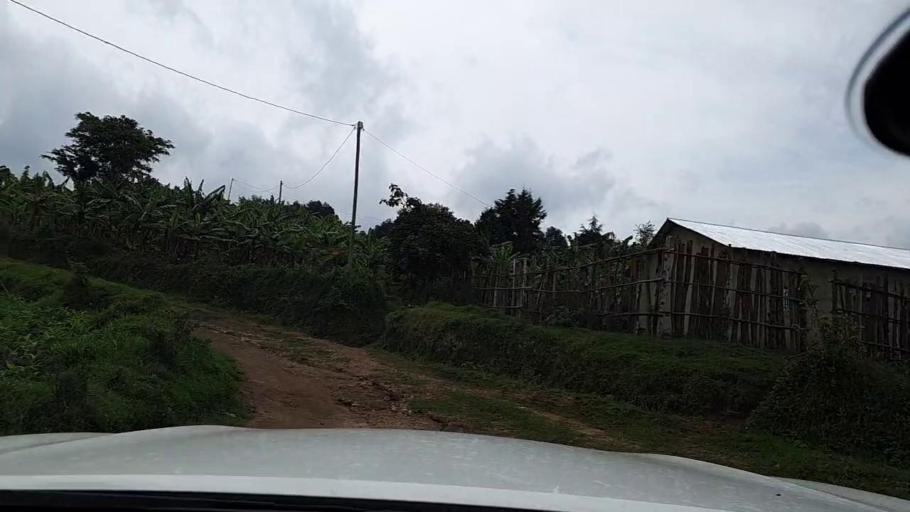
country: RW
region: Western Province
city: Kibuye
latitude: -2.1980
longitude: 29.3192
